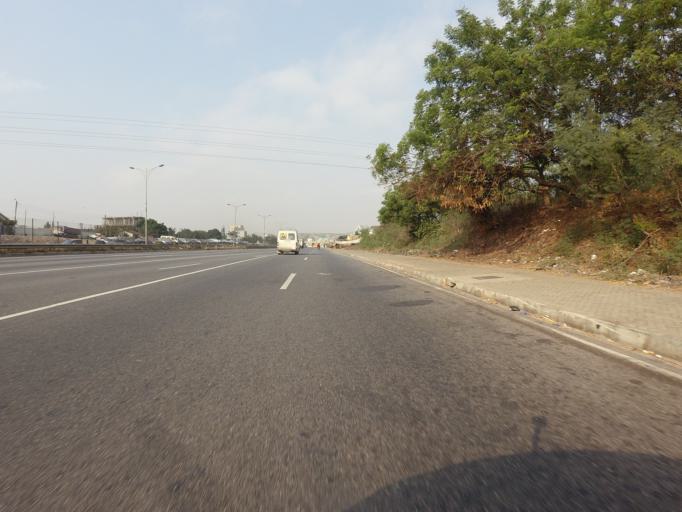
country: GH
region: Greater Accra
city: Dome
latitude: 5.6148
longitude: -0.2191
